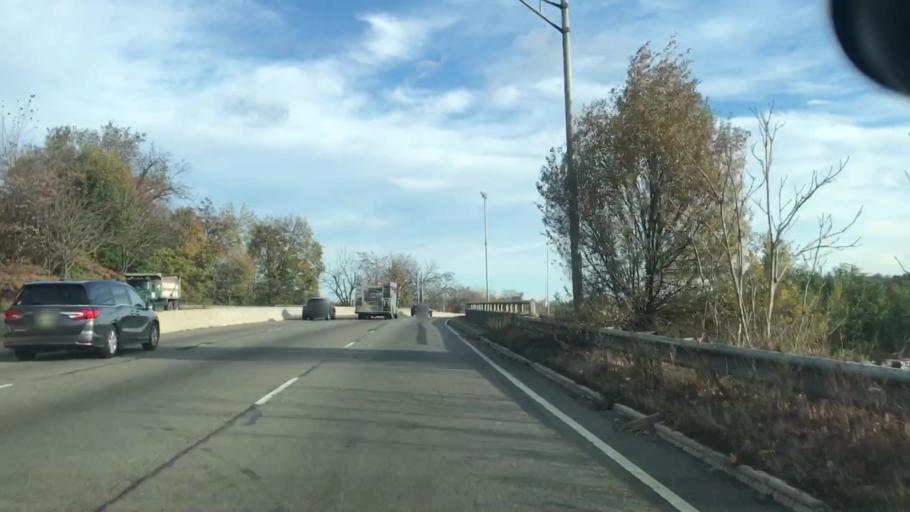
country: US
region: New Jersey
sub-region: Hudson County
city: Kearny
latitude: 40.7680
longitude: -74.1593
